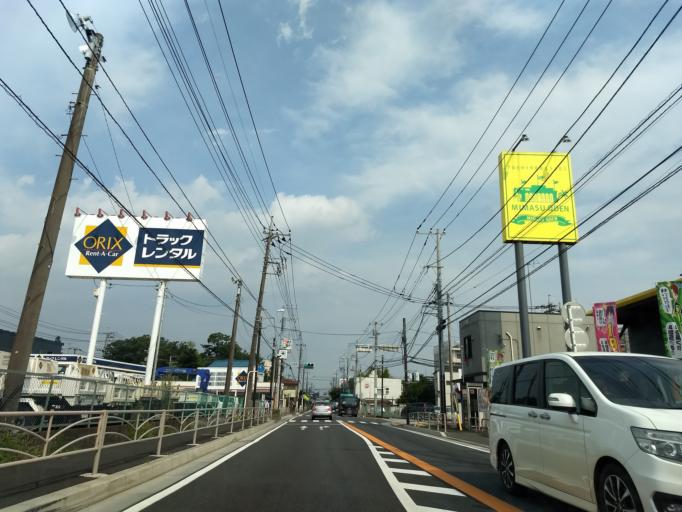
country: JP
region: Kanagawa
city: Minami-rinkan
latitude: 35.4946
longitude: 139.5066
